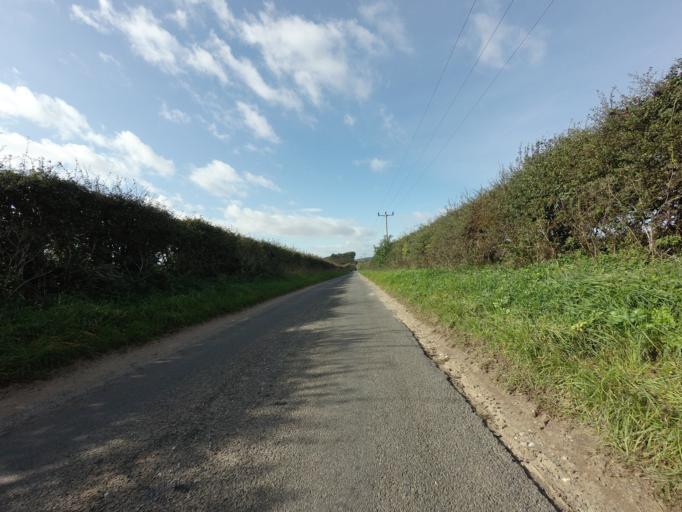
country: GB
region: England
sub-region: Norfolk
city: Hunstanton
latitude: 52.9358
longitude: 0.6399
